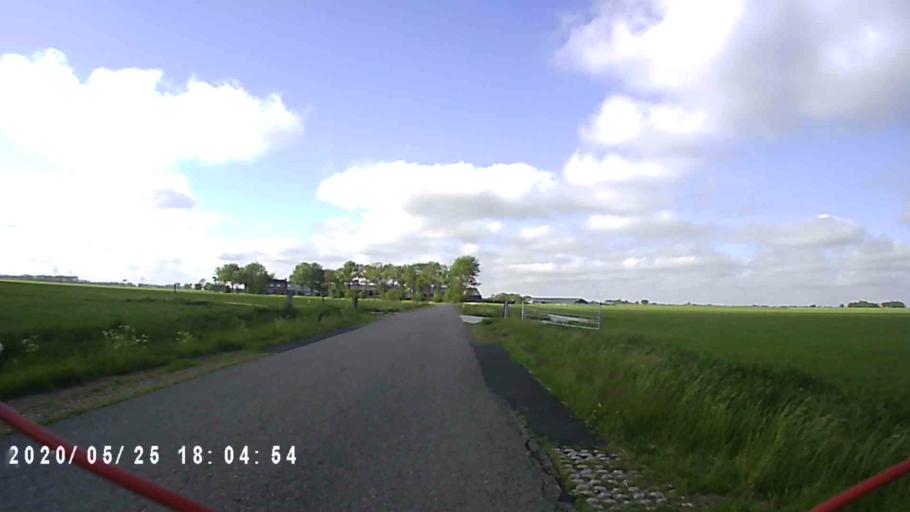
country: NL
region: Groningen
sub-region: Gemeente Winsum
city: Winsum
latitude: 53.2913
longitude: 6.4941
